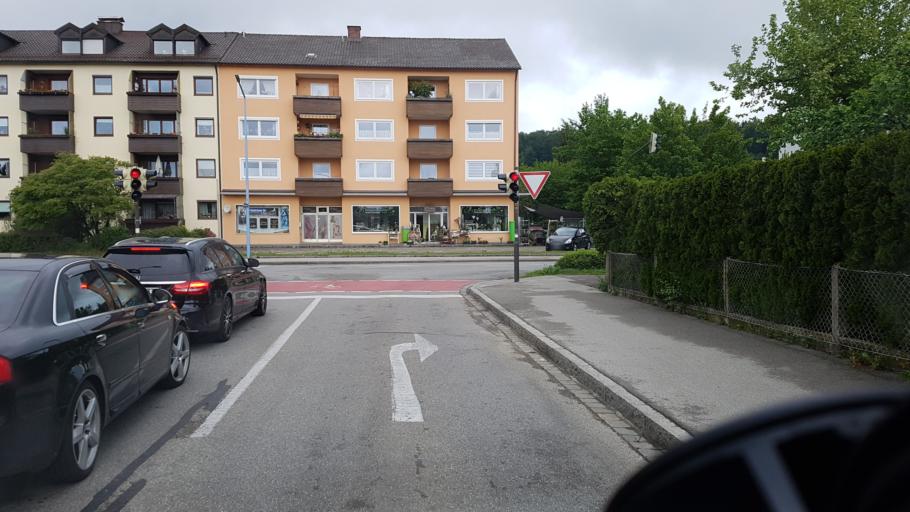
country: DE
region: Bavaria
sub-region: Upper Bavaria
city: Burghausen
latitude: 48.1690
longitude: 12.8170
